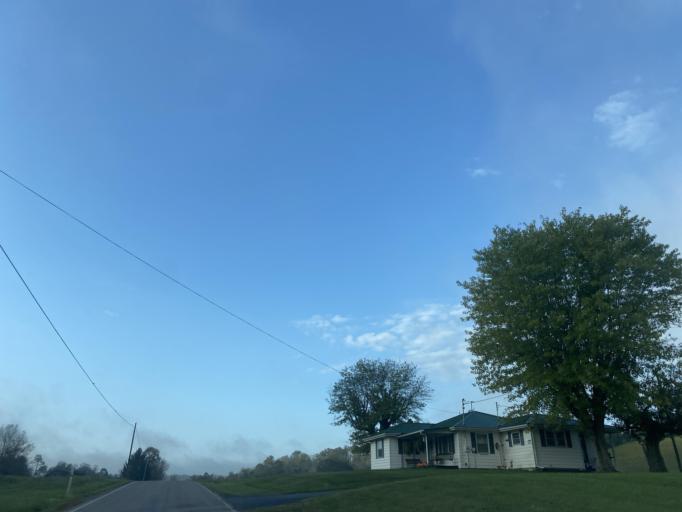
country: US
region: Kentucky
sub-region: Pendleton County
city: Falmouth
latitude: 38.7311
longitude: -84.3168
